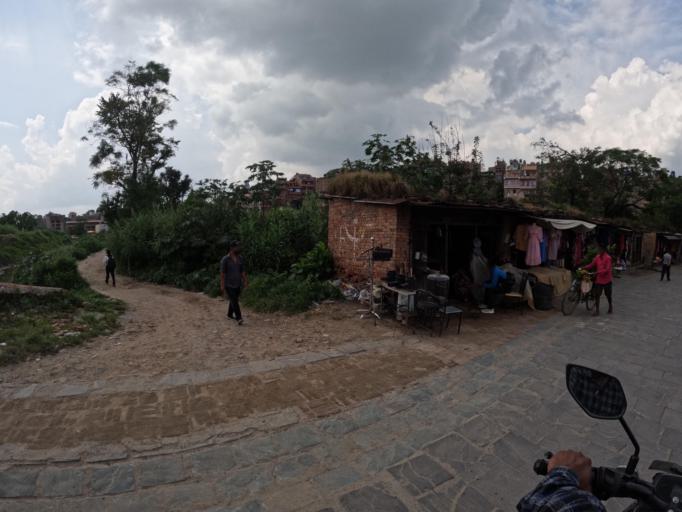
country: NP
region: Central Region
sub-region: Bagmati Zone
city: Bhaktapur
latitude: 27.6681
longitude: 85.4272
